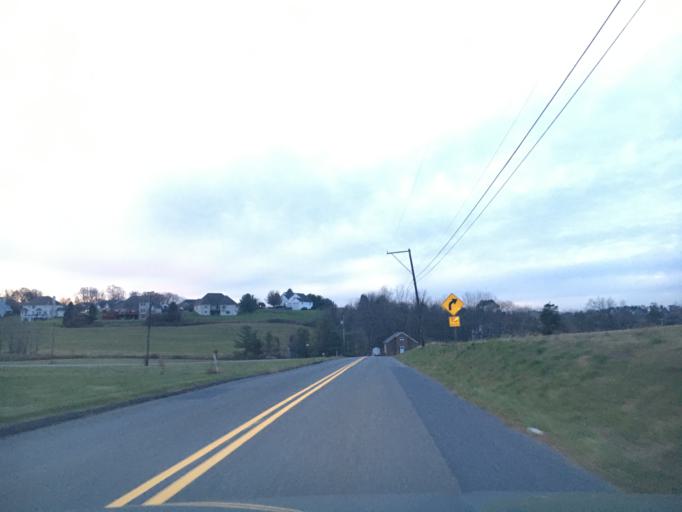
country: US
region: Pennsylvania
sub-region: Lehigh County
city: Schnecksville
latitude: 40.6953
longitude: -75.5810
